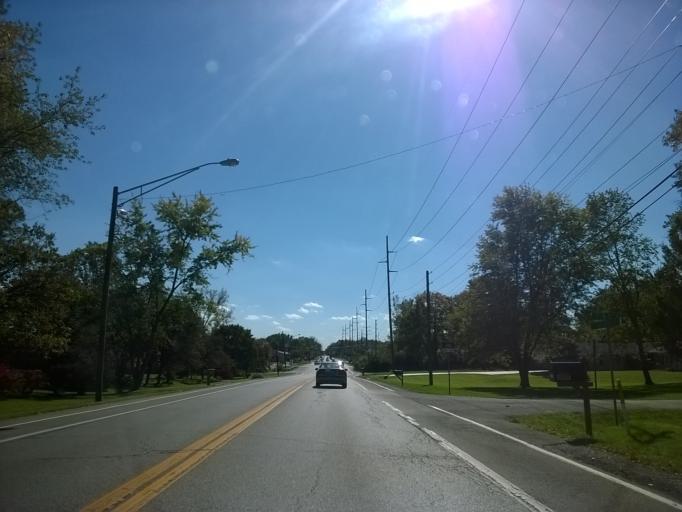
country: US
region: Indiana
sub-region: Marion County
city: Broad Ripple
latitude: 39.8717
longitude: -86.0955
